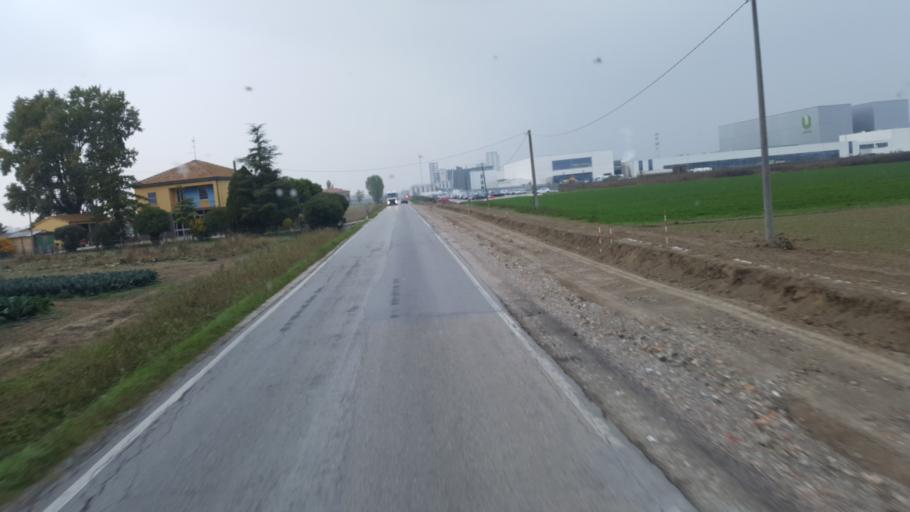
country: IT
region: Emilia-Romagna
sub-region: Provincia di Ravenna
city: Lavezzola
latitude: 44.5329
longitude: 11.8682
